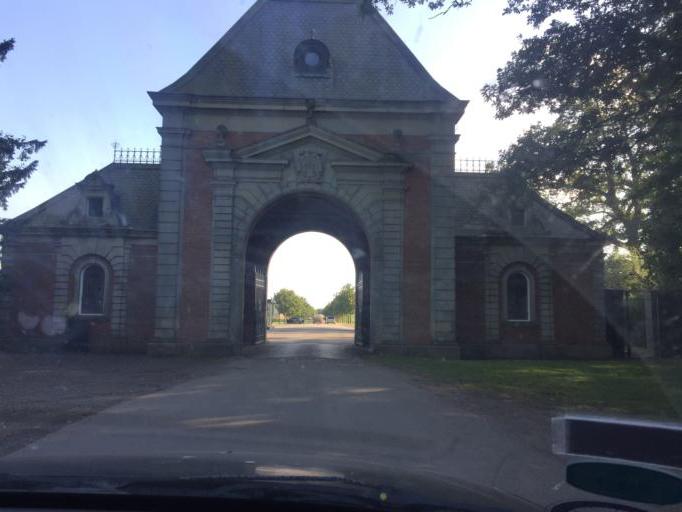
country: DK
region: Zealand
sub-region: Lolland Kommune
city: Maribo
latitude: 54.8116
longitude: 11.5109
